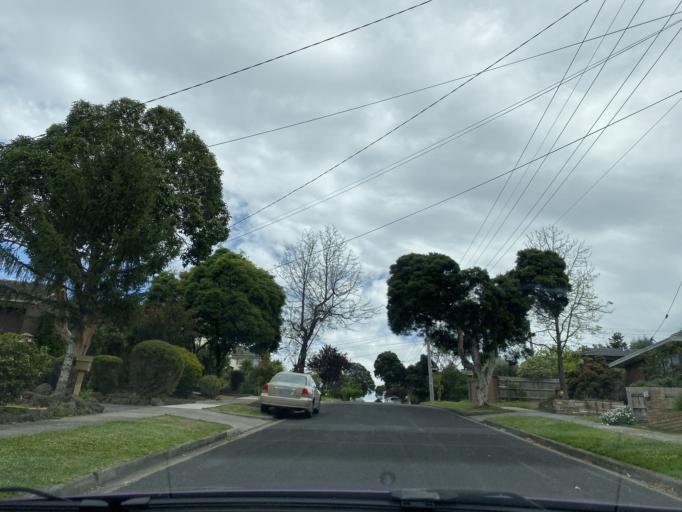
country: AU
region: Victoria
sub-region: Manningham
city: Templestowe Lower
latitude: -37.7649
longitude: 145.1234
